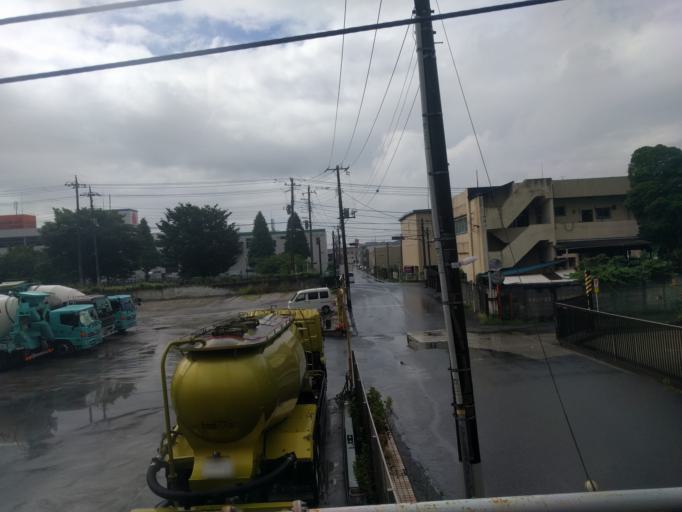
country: JP
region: Kanagawa
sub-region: Kawasaki-shi
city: Kawasaki
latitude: 35.5351
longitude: 139.7167
